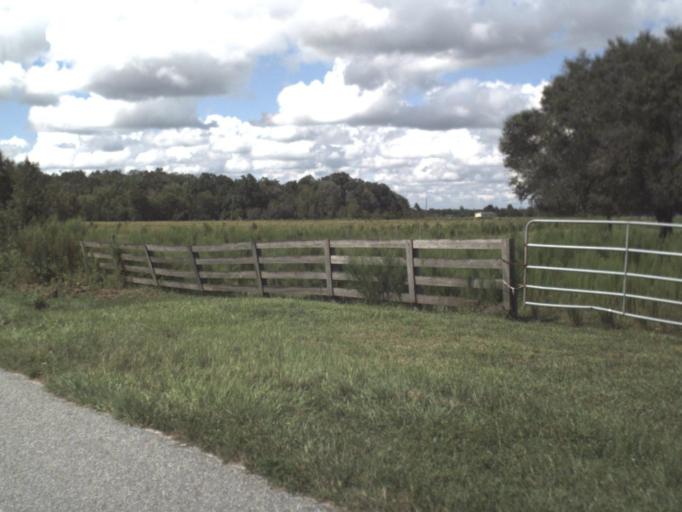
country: US
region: Florida
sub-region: DeSoto County
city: Arcadia
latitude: 27.3150
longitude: -82.1091
